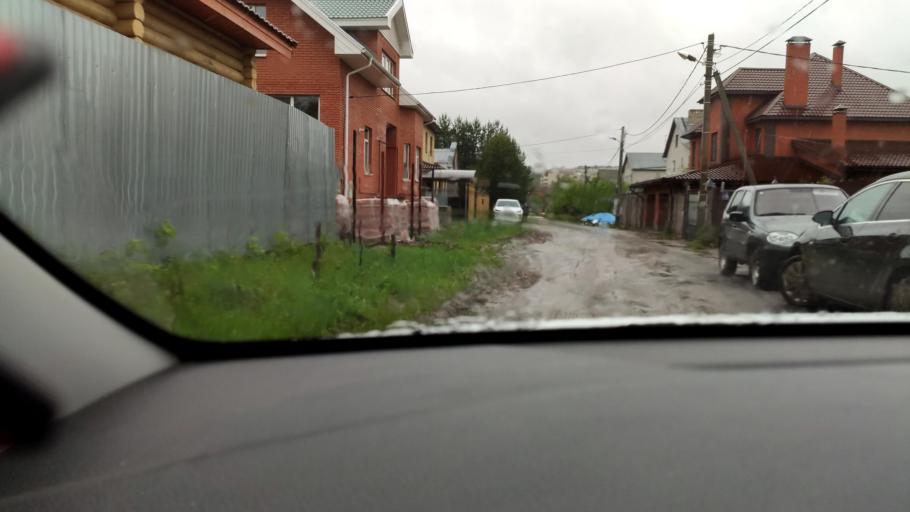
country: RU
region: Tatarstan
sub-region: Gorod Kazan'
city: Kazan
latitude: 55.8090
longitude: 49.2126
